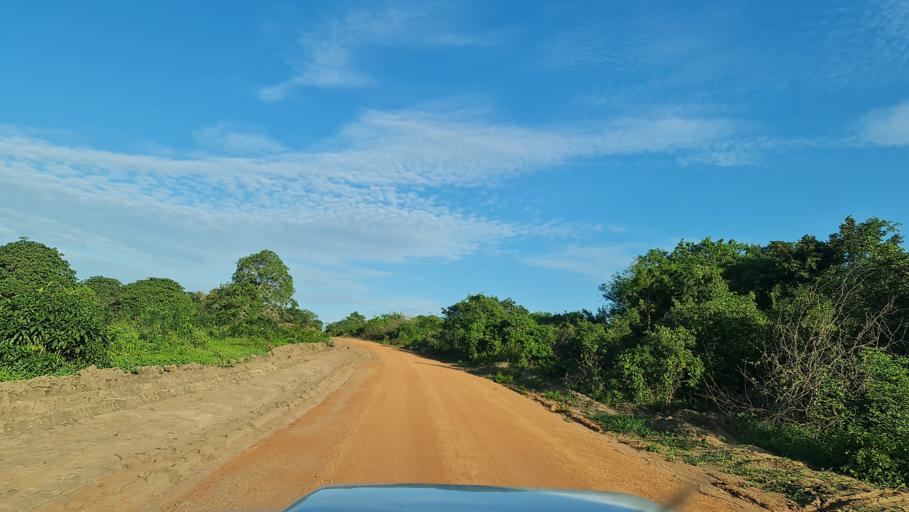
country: MZ
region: Nampula
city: Nacala
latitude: -14.6717
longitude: 40.2747
